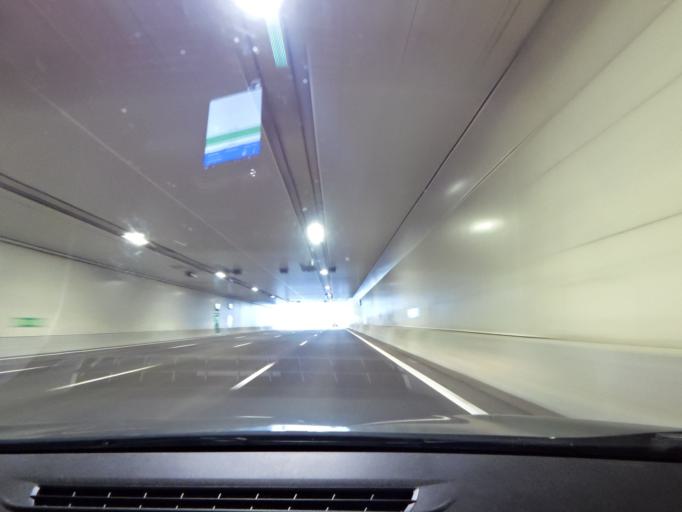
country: NL
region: South Holland
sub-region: Gemeente Vlaardingen
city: Vlaardingen
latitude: 51.9426
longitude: 4.3590
